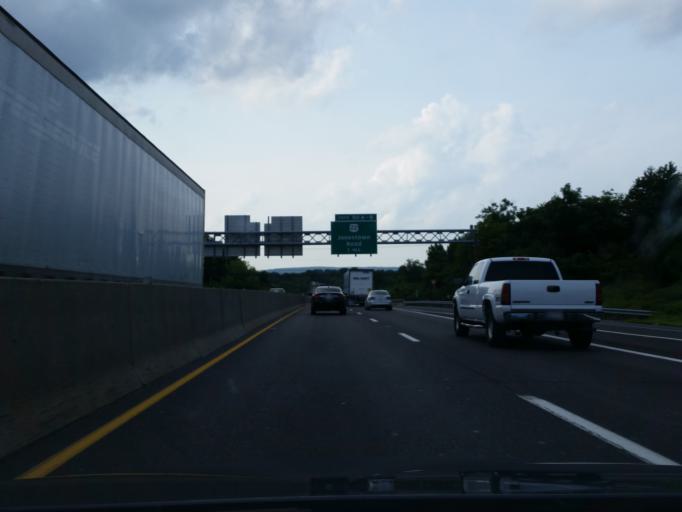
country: US
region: Pennsylvania
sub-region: Dauphin County
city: Progress
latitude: 40.2808
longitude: -76.8196
